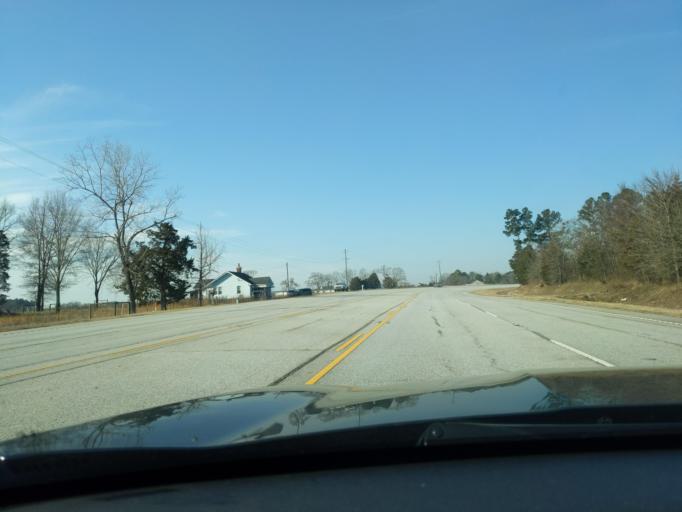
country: US
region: South Carolina
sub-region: Abbeville County
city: Calhoun Falls
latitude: 34.0952
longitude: -82.5680
